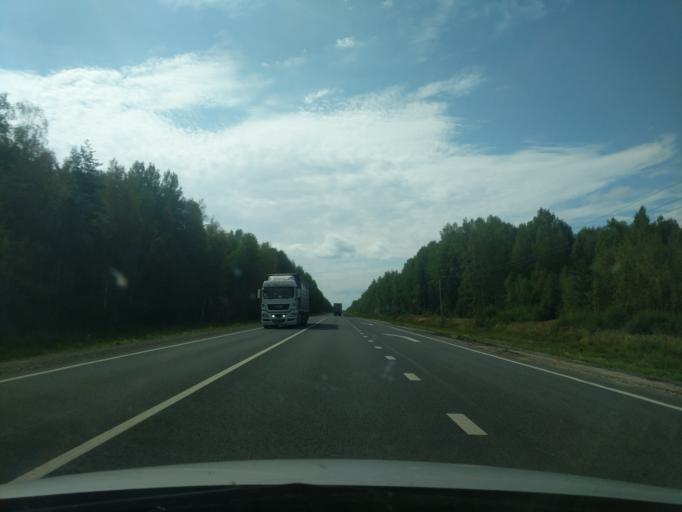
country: RU
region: Kostroma
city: Kadyy
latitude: 57.8150
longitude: 43.2320
